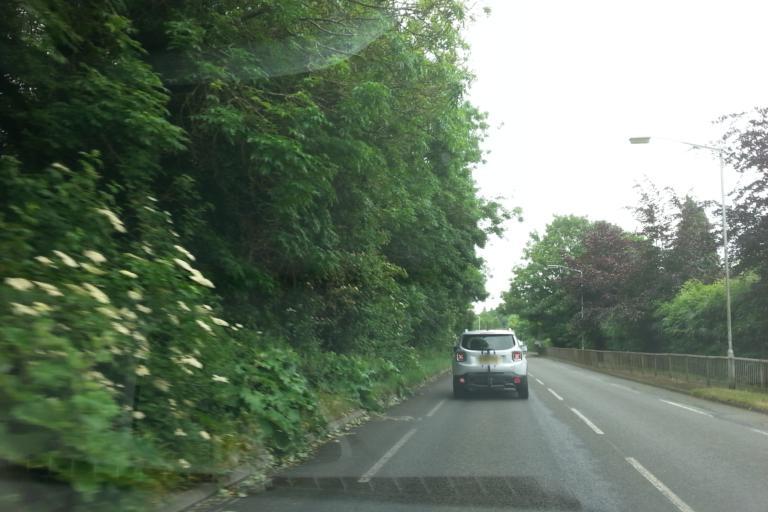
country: GB
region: England
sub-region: Peterborough
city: Peterborough
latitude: 52.5544
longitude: -0.2878
